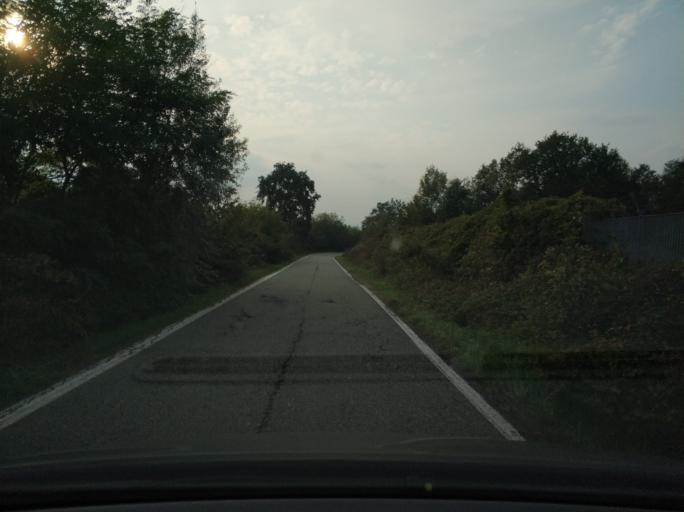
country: IT
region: Piedmont
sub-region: Provincia di Torino
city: Rivarossa
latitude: 45.2405
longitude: 7.6872
